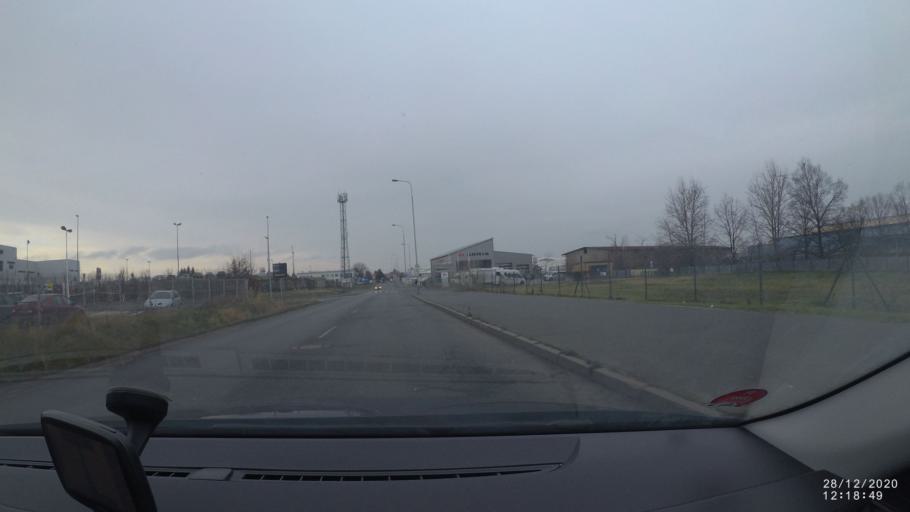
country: CZ
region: Central Bohemia
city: Brandys nad Labem-Stara Boleslav
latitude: 50.1760
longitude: 14.6605
